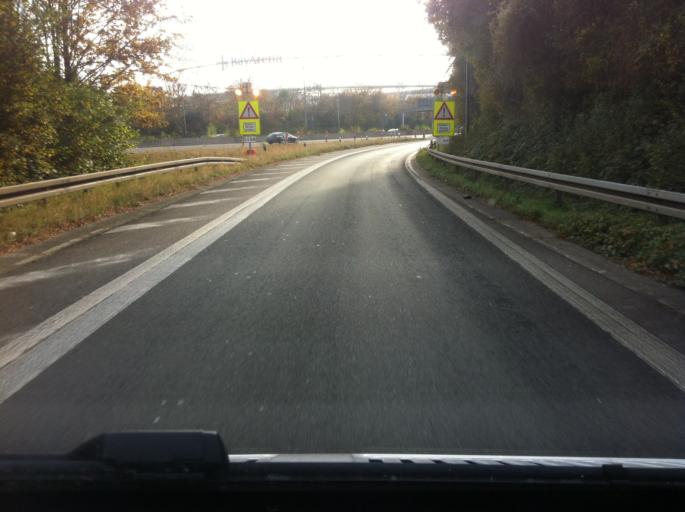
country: DE
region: North Rhine-Westphalia
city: Opladen
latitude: 51.0417
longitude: 7.0047
